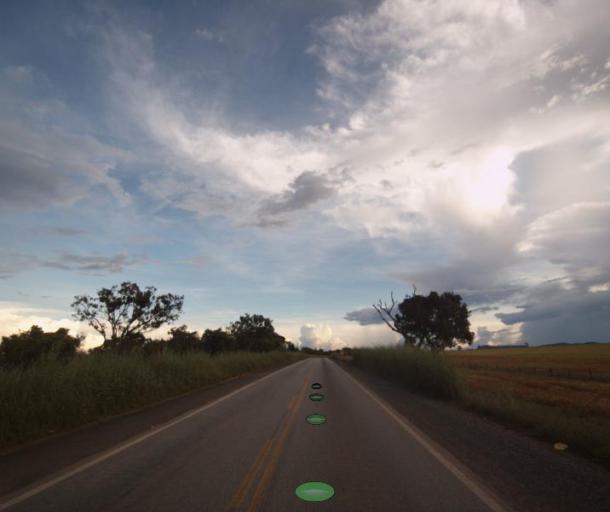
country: BR
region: Goias
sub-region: Uruacu
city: Uruacu
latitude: -14.1101
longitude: -49.1039
